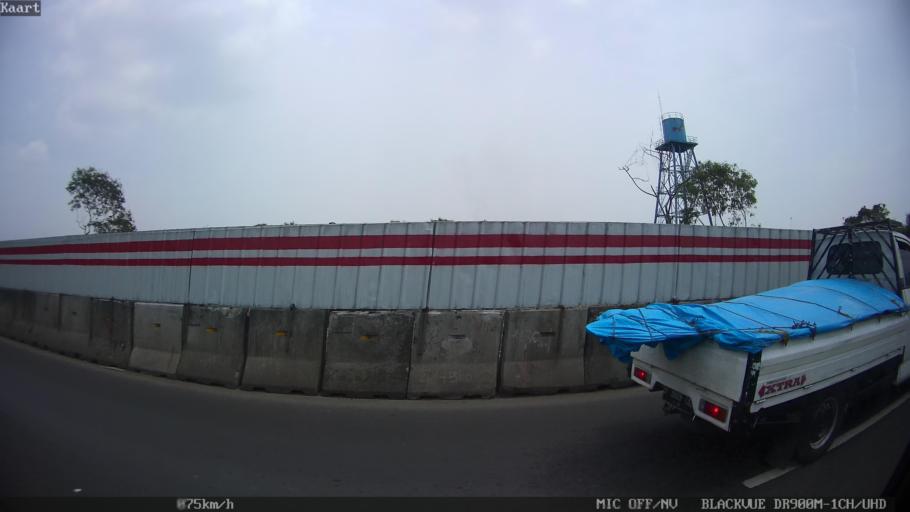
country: ID
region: West Java
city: Kresek
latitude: -6.1716
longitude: 106.3345
